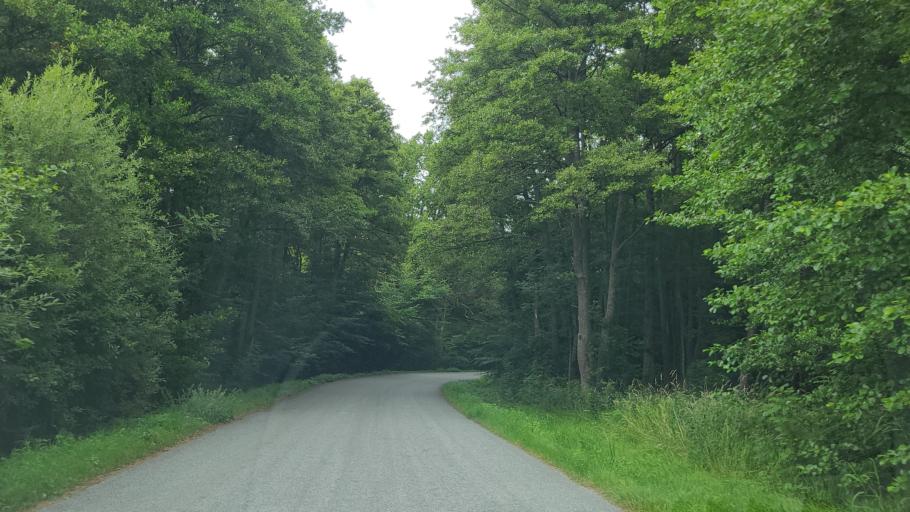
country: SE
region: Stockholm
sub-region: Upplands-Bro Kommun
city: Bro
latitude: 59.4802
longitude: 17.5650
